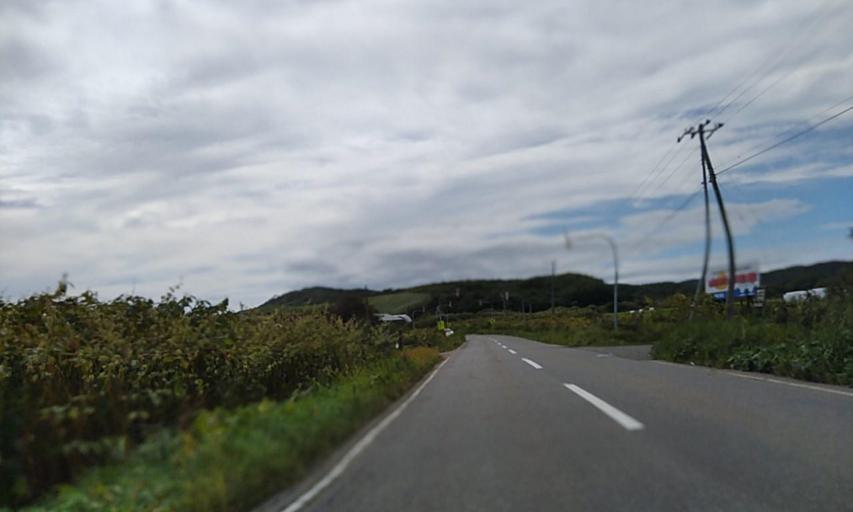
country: JP
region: Hokkaido
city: Obihiro
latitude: 42.7868
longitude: 143.7903
